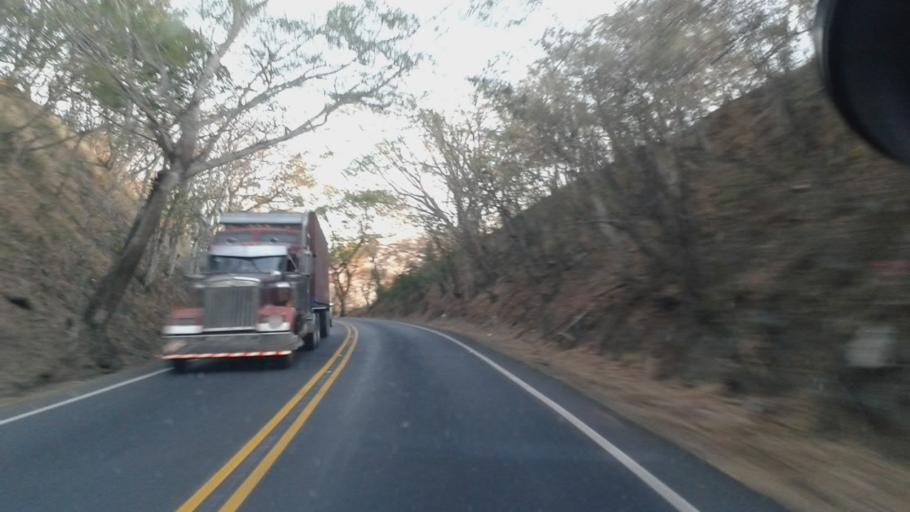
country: CR
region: Puntarenas
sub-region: Canton Central de Puntarenas
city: Puntarenas
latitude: 10.1213
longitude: -84.8987
